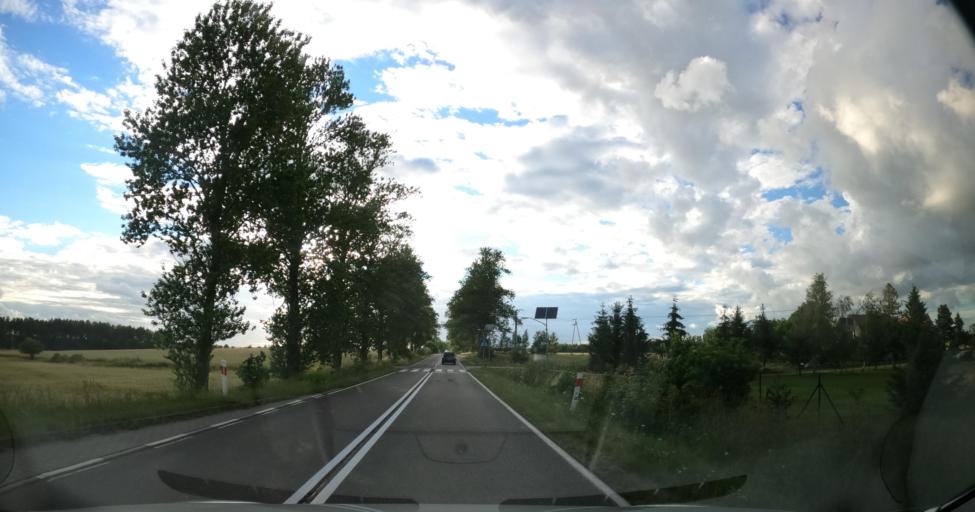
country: PL
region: Pomeranian Voivodeship
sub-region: Powiat slupski
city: Damnica
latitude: 54.4338
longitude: 17.3556
